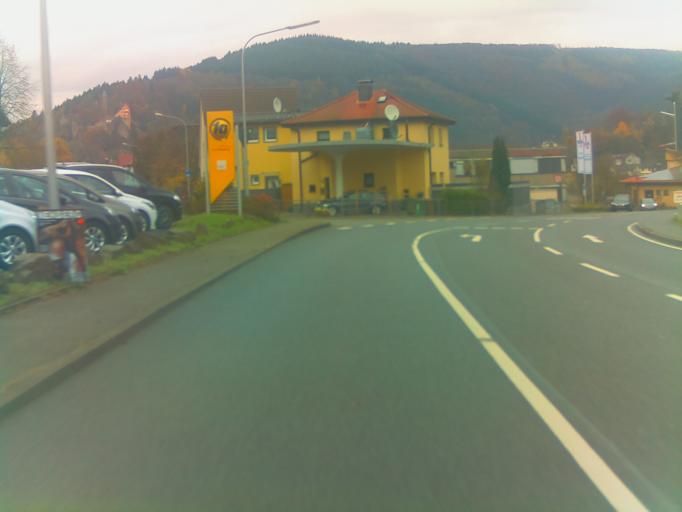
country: DE
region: Hesse
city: Hirschhorn
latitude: 49.4389
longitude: 8.8960
